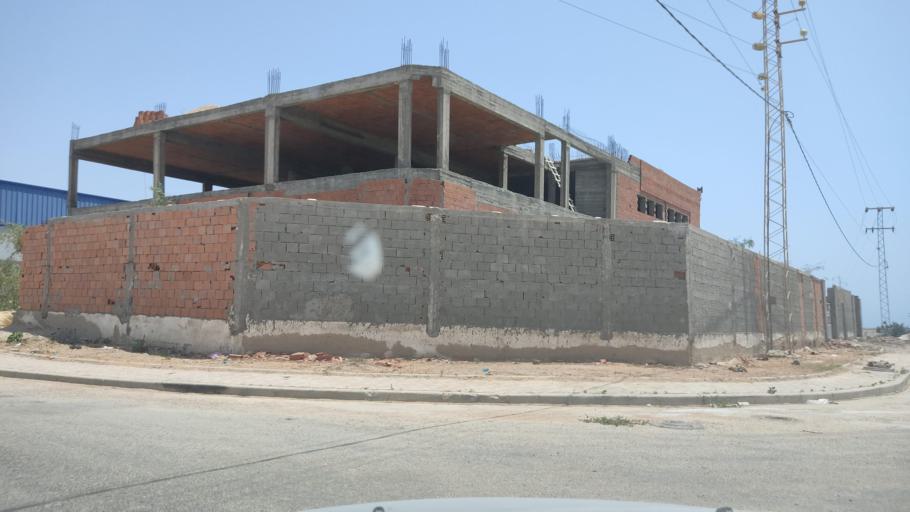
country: TN
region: Safaqis
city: Sfax
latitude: 34.6604
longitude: 10.6996
